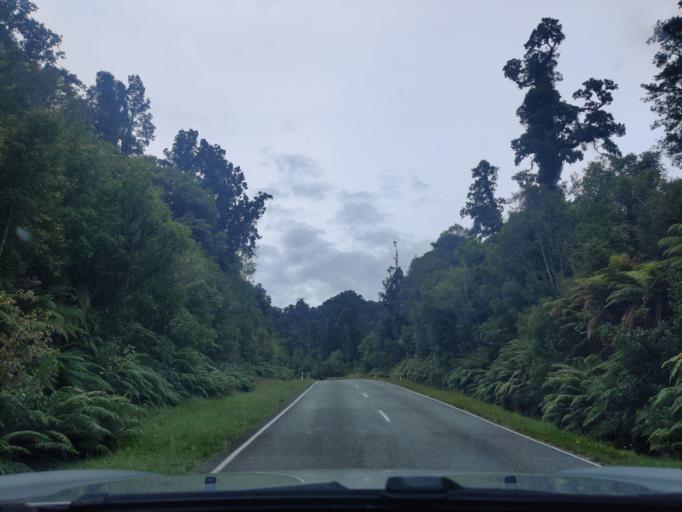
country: NZ
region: West Coast
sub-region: Westland District
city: Hokitika
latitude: -42.9470
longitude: 170.7543
